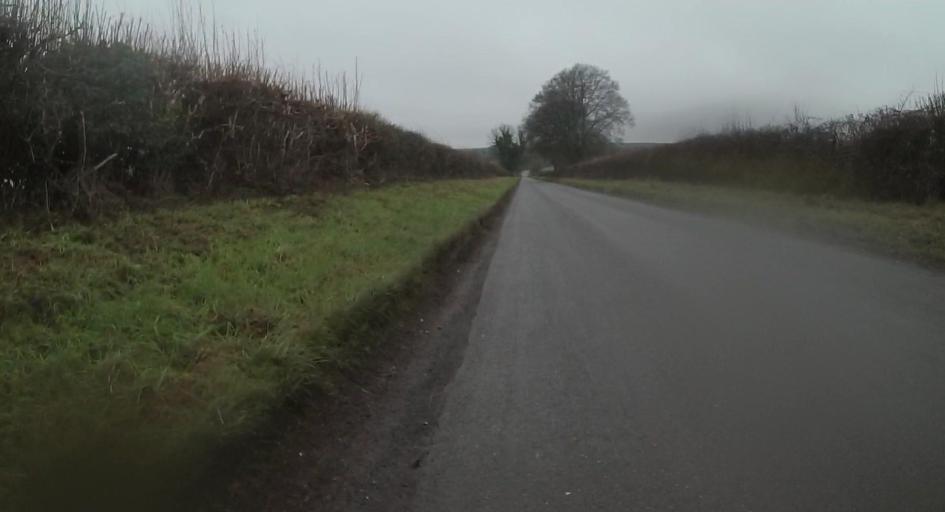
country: GB
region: England
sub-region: Hampshire
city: Kings Worthy
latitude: 51.1316
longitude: -1.2147
